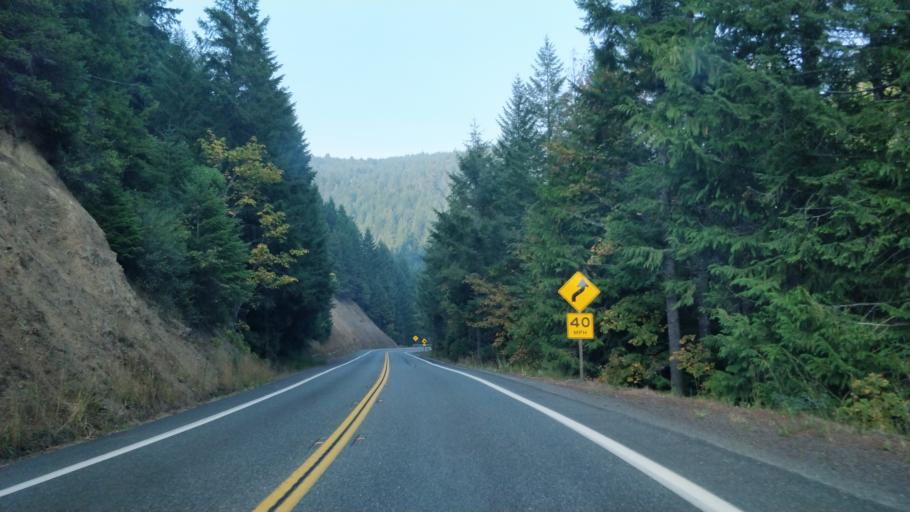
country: US
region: California
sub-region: Humboldt County
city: Willow Creek
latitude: 40.9053
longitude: -123.7572
